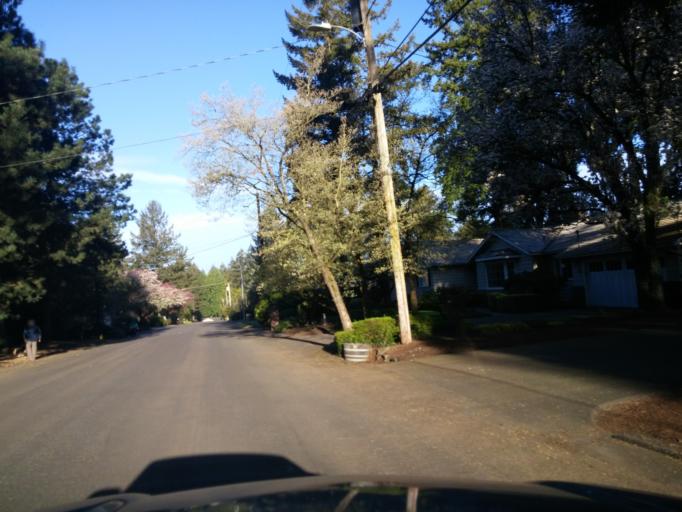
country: US
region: Oregon
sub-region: Washington County
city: West Slope
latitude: 45.5013
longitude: -122.7814
